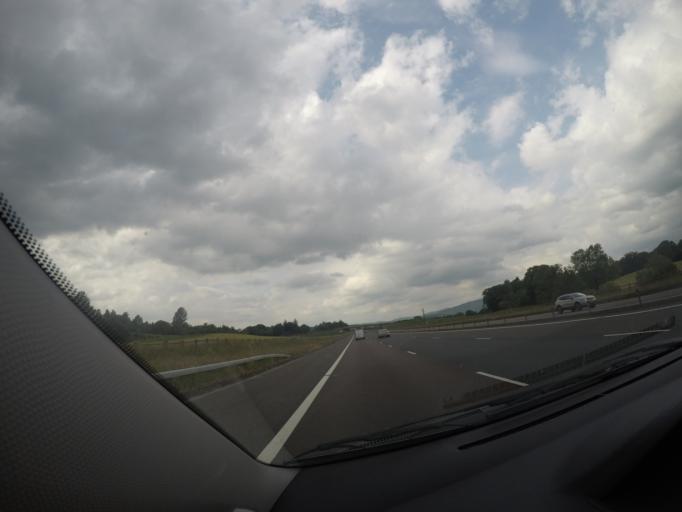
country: GB
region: Scotland
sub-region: Dumfries and Galloway
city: Moffat
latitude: 55.2980
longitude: -3.4427
